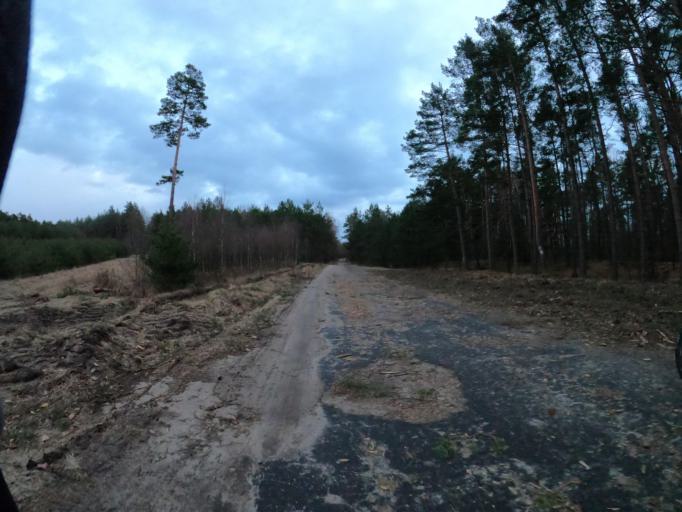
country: PL
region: West Pomeranian Voivodeship
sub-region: Powiat szczecinecki
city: Borne Sulinowo
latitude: 53.5464
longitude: 16.5834
